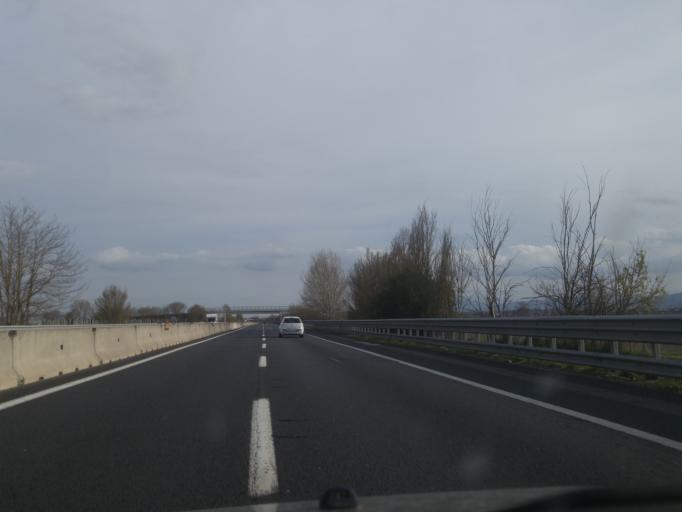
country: IT
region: Tuscany
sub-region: Provincia di Siena
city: Bettolle
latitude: 43.1780
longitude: 11.8314
